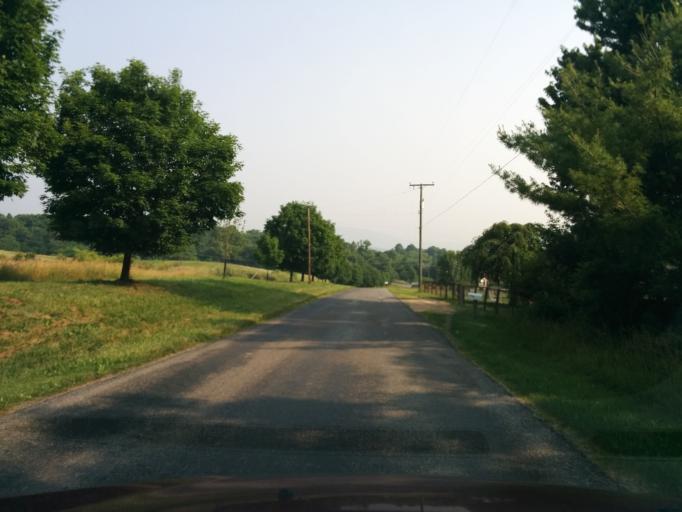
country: US
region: Virginia
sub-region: City of Lexington
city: Lexington
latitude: 37.7695
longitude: -79.4373
